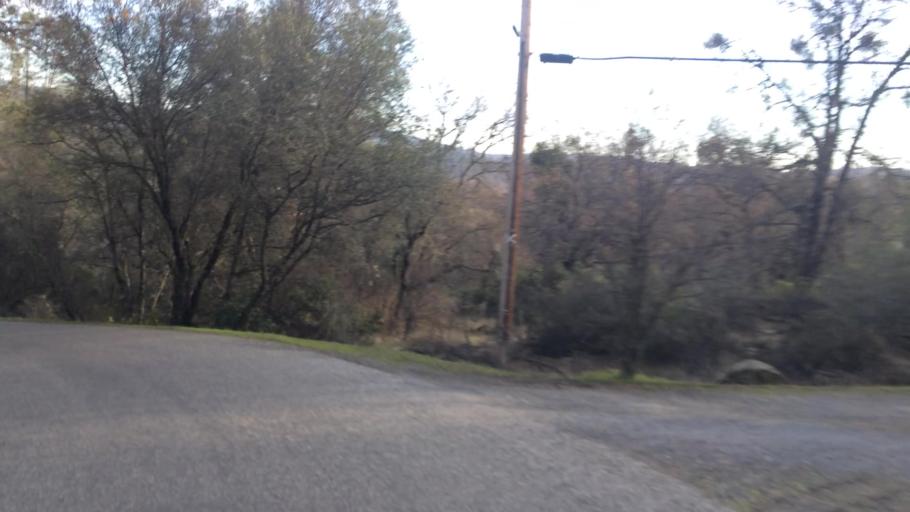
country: US
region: California
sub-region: Nevada County
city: Penn Valley
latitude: 39.2109
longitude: -121.1757
